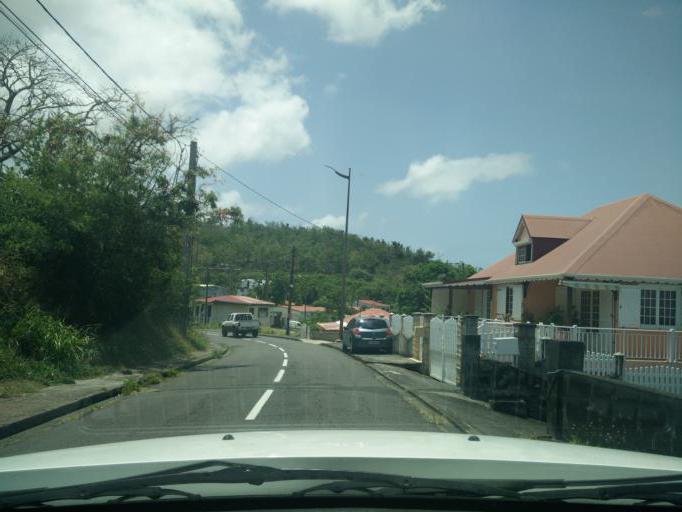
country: GP
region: Guadeloupe
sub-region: Guadeloupe
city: Gourbeyre
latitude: 15.9494
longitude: -61.7002
